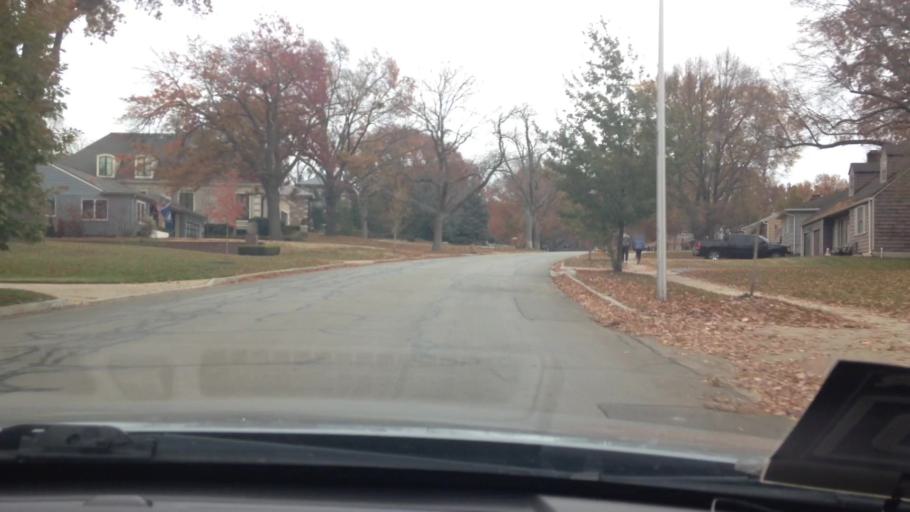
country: US
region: Kansas
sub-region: Johnson County
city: Prairie Village
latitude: 39.0000
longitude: -94.6262
